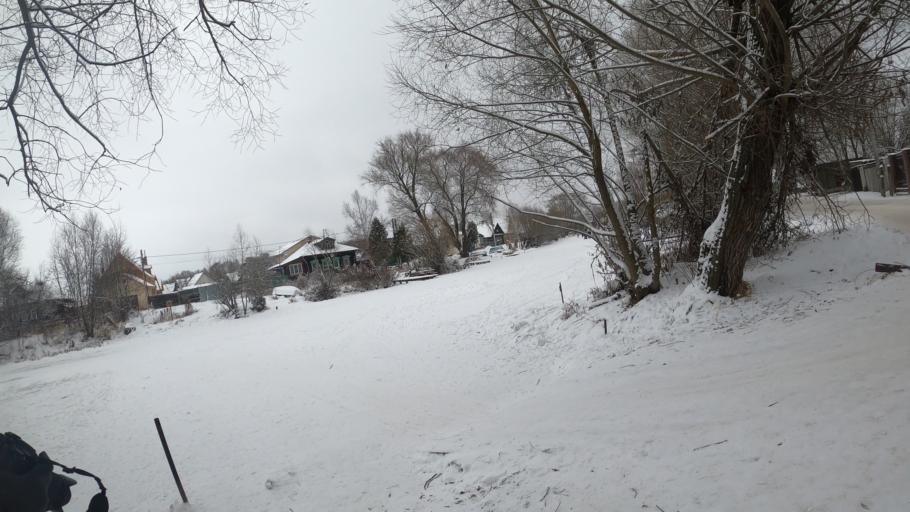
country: RU
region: Jaroslavl
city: Pereslavl'-Zalesskiy
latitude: 56.7343
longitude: 38.8308
